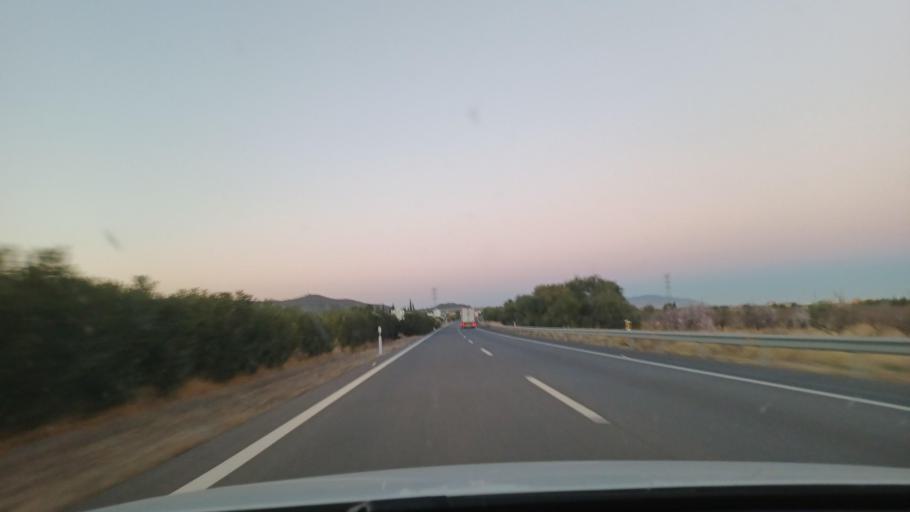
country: ES
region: Valencia
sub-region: Provincia de Castello
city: Orpesa/Oropesa del Mar
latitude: 40.1459
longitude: 0.1450
